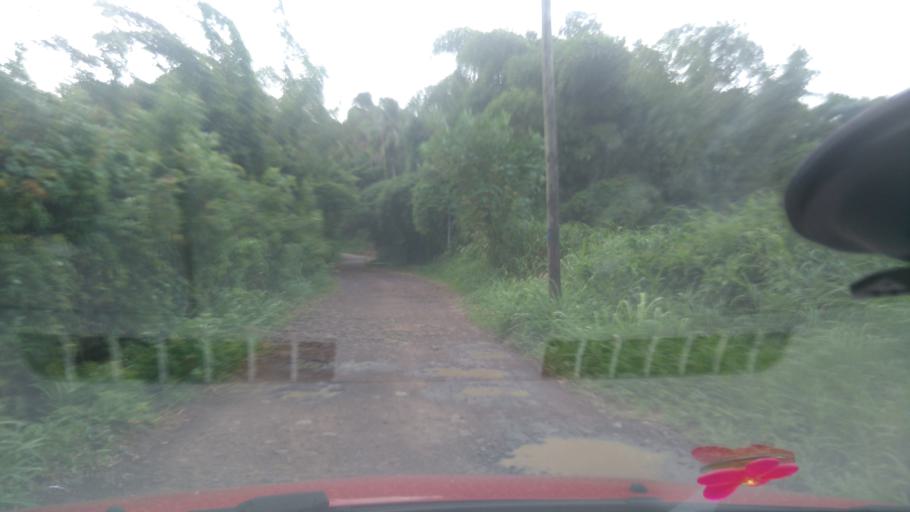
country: MQ
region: Martinique
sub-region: Martinique
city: Ducos
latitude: 14.5529
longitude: -60.9677
